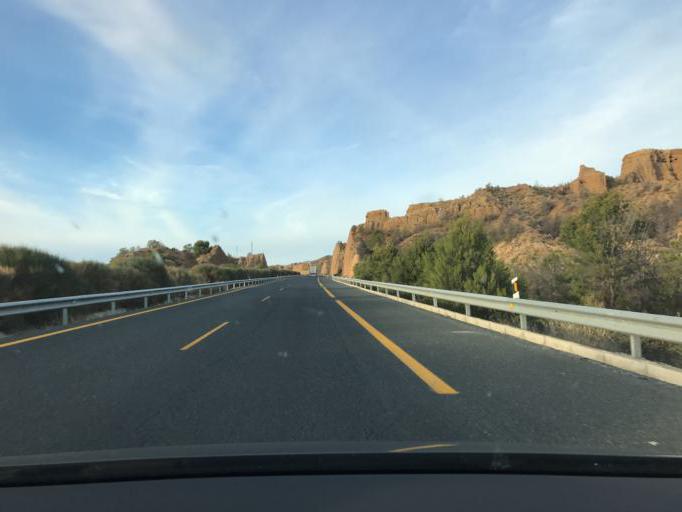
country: ES
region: Andalusia
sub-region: Provincia de Granada
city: Guadix
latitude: 37.3101
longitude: -3.1122
